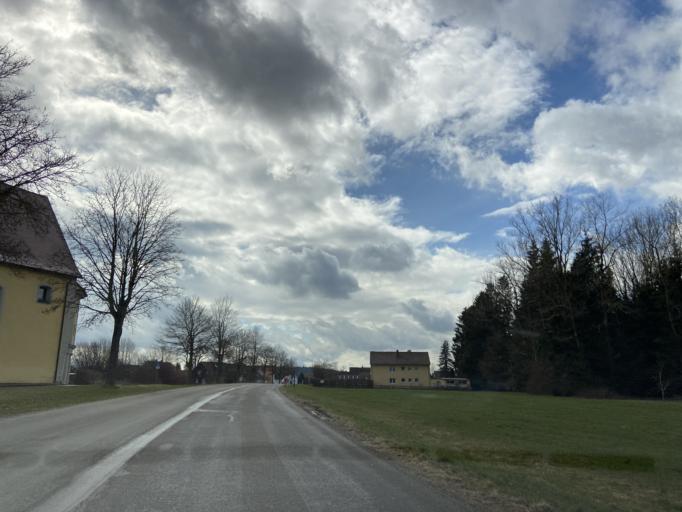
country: DE
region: Baden-Wuerttemberg
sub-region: Tuebingen Region
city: Pfullendorf
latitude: 47.9310
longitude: 9.2602
